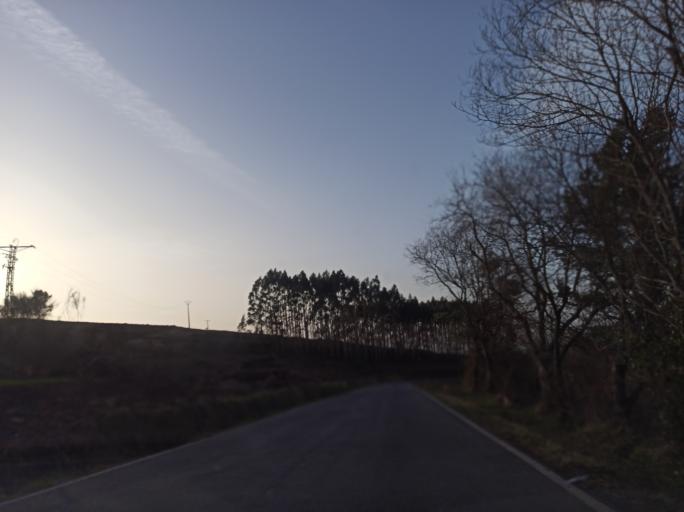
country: ES
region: Galicia
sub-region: Provincia da Coruna
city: Sobrado
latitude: 43.0324
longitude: -7.9349
